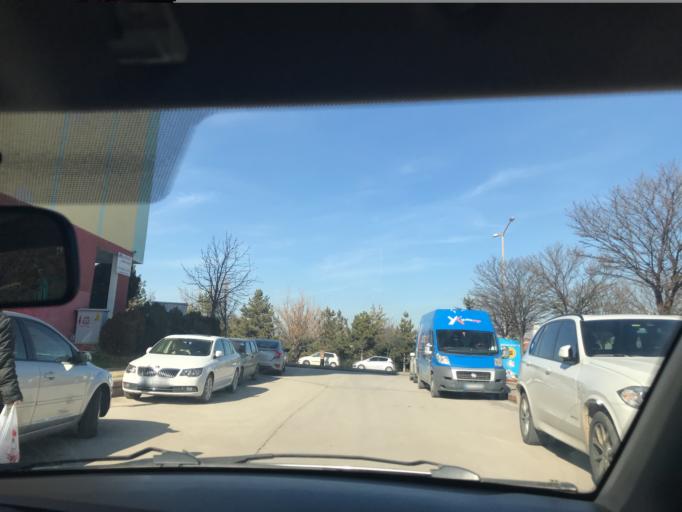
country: TR
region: Ankara
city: Batikent
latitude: 39.9705
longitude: 32.7275
